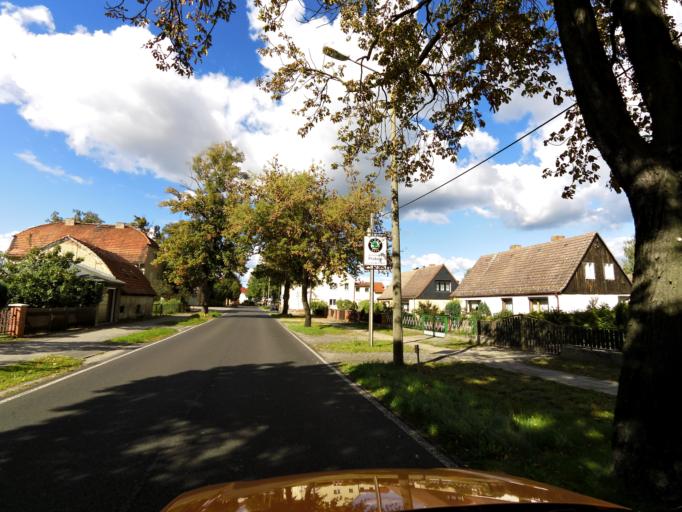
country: DE
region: Brandenburg
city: Luckenwalde
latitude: 52.0804
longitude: 13.1818
